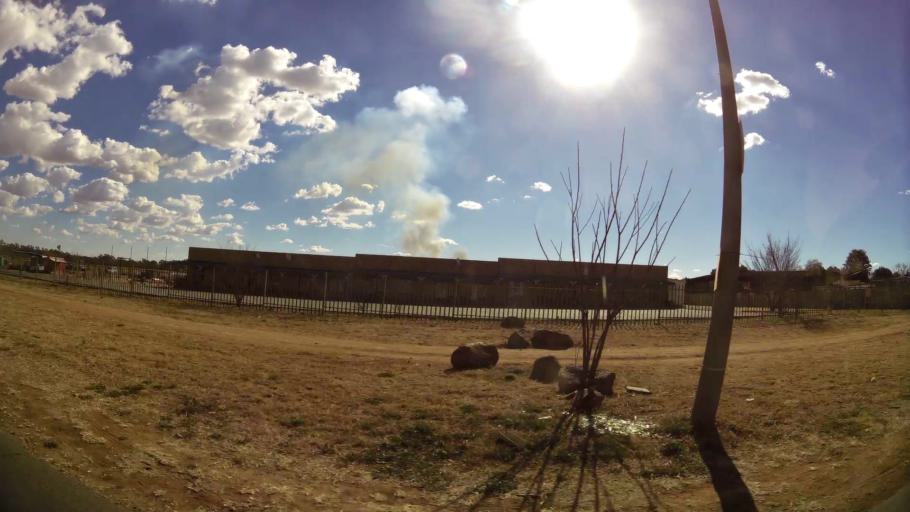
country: ZA
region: North-West
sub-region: Dr Kenneth Kaunda District Municipality
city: Klerksdorp
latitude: -26.8473
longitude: 26.6527
